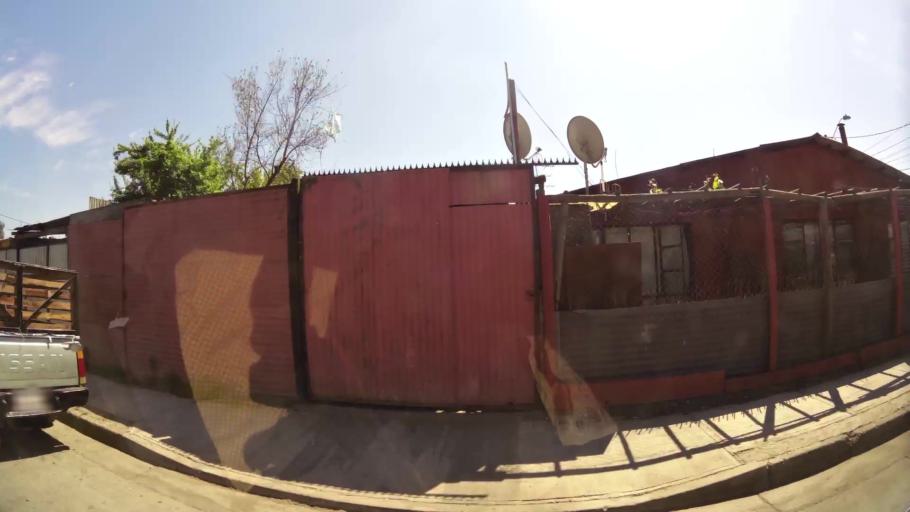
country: CL
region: Santiago Metropolitan
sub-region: Provincia de Talagante
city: Talagante
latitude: -33.6549
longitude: -70.9263
